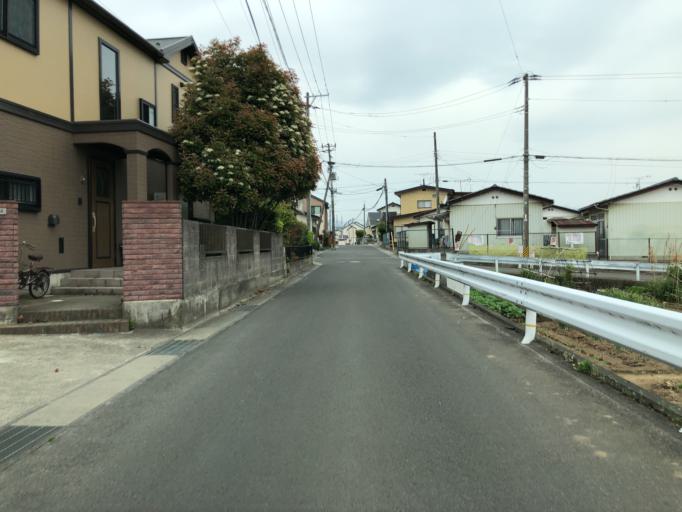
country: JP
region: Fukushima
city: Fukushima-shi
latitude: 37.7876
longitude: 140.4757
